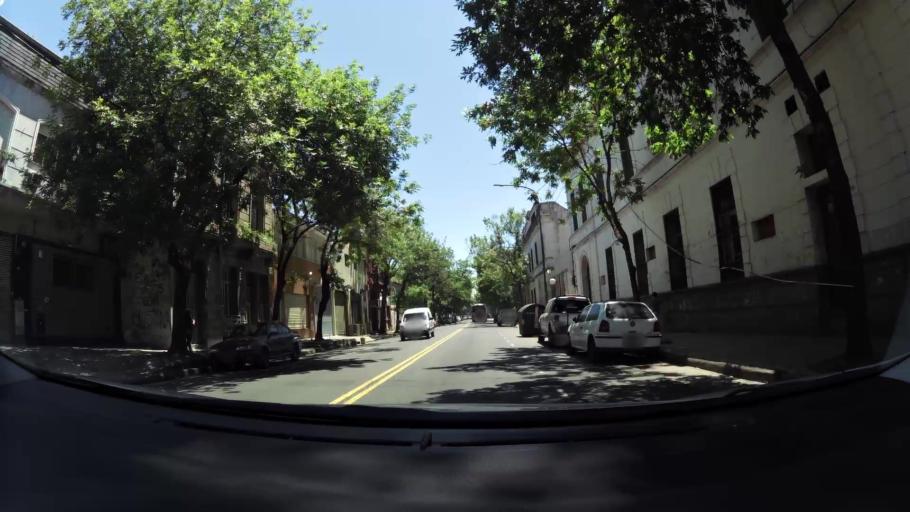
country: AR
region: Buenos Aires
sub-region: Partido de Avellaneda
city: Avellaneda
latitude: -34.6515
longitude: -58.3762
